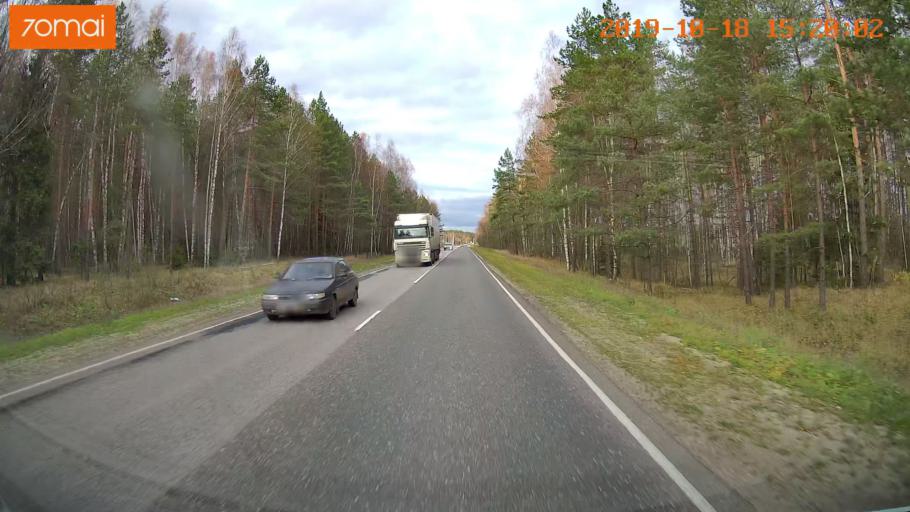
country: RU
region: Vladimir
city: Anopino
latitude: 55.6818
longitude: 40.7421
